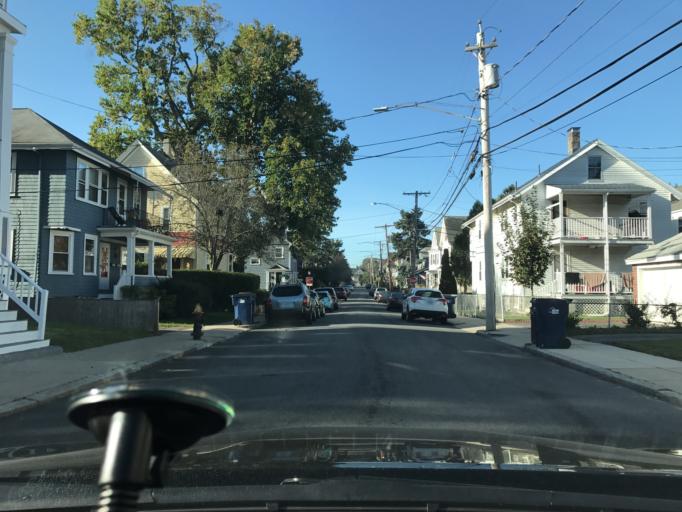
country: US
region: Massachusetts
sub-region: Suffolk County
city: Jamaica Plain
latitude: 42.2920
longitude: -71.1343
